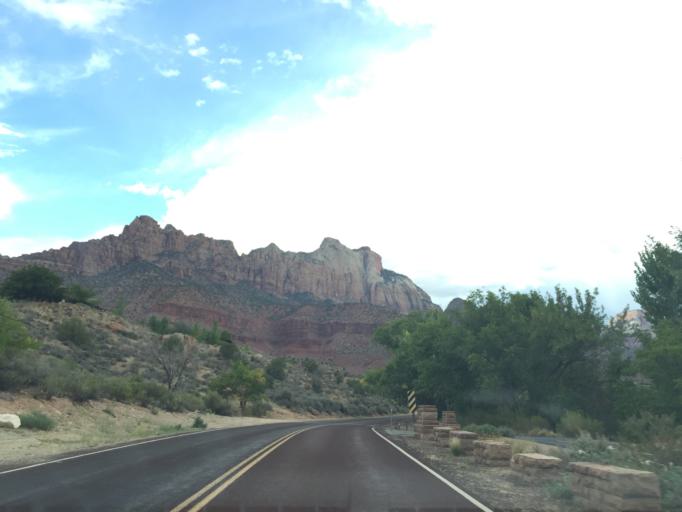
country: US
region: Utah
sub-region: Washington County
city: Hildale
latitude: 37.1707
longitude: -113.0134
